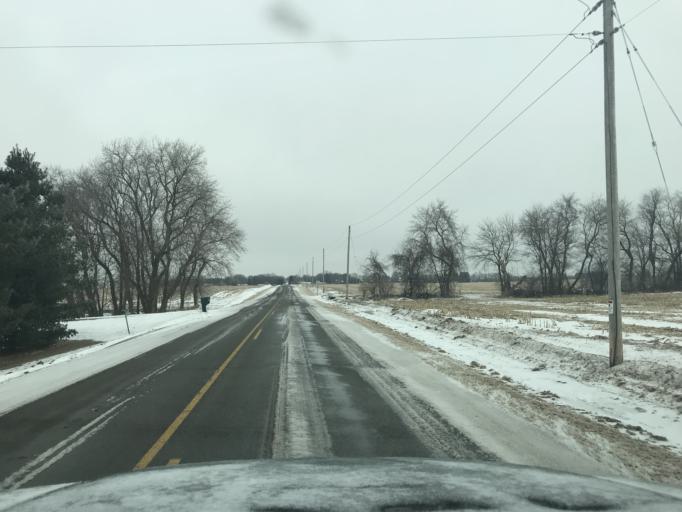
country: US
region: Wisconsin
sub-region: Dane County
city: Cottage Grove
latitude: 43.0963
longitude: -89.2296
